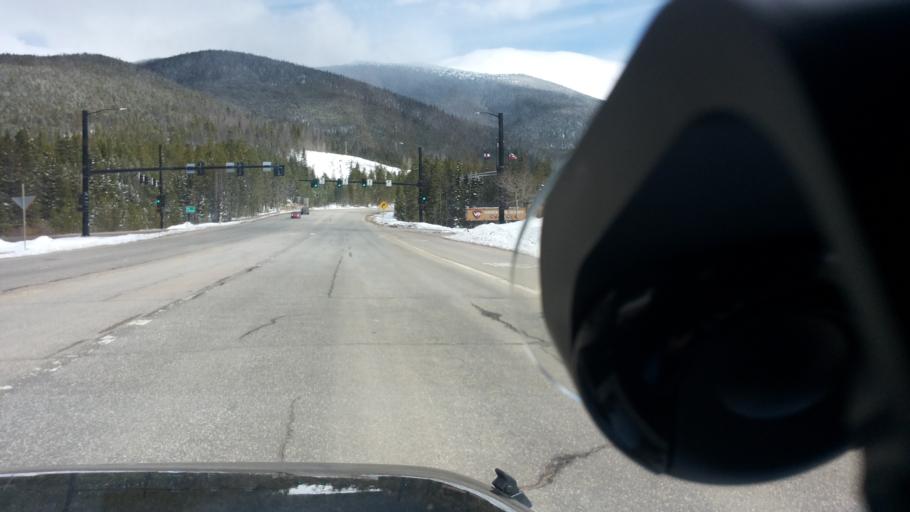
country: US
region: Colorado
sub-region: Grand County
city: Fraser
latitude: 39.8824
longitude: -105.7566
